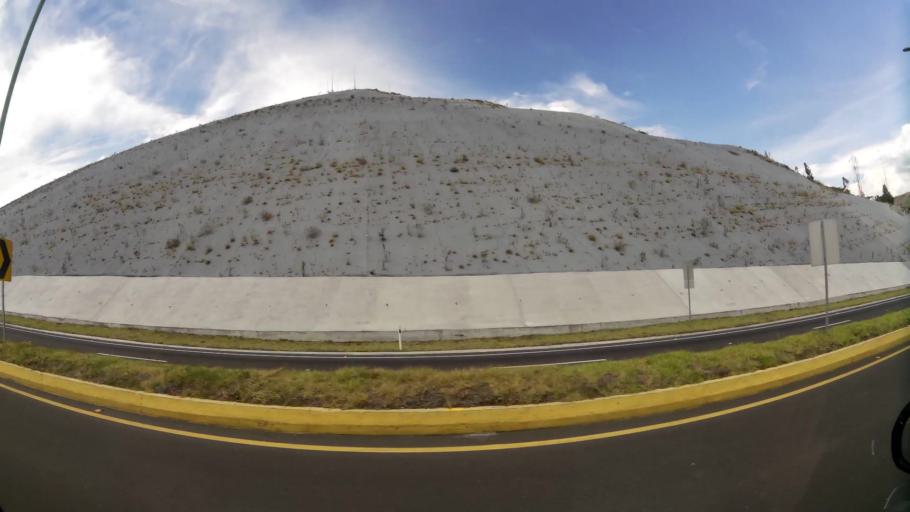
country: EC
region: Pichincha
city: Quito
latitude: -0.1003
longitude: -78.3726
